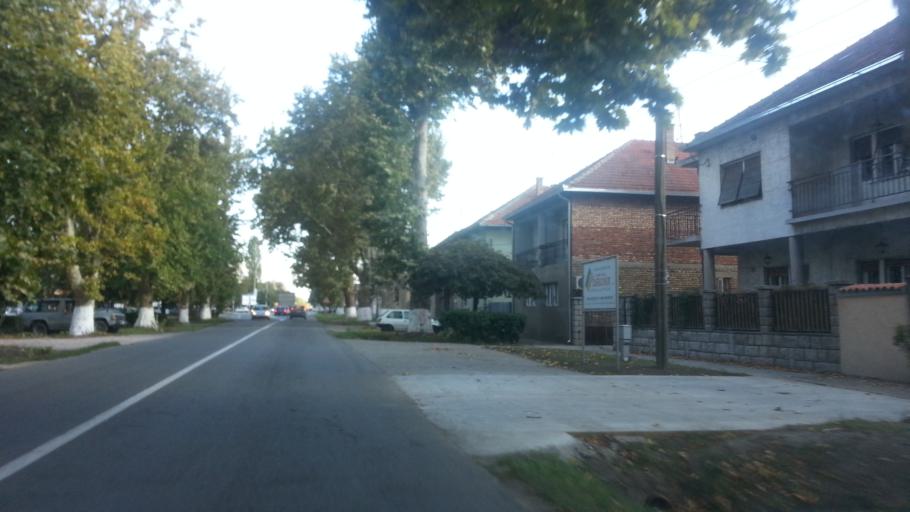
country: RS
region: Autonomna Pokrajina Vojvodina
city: Nova Pazova
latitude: 44.9506
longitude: 20.2099
